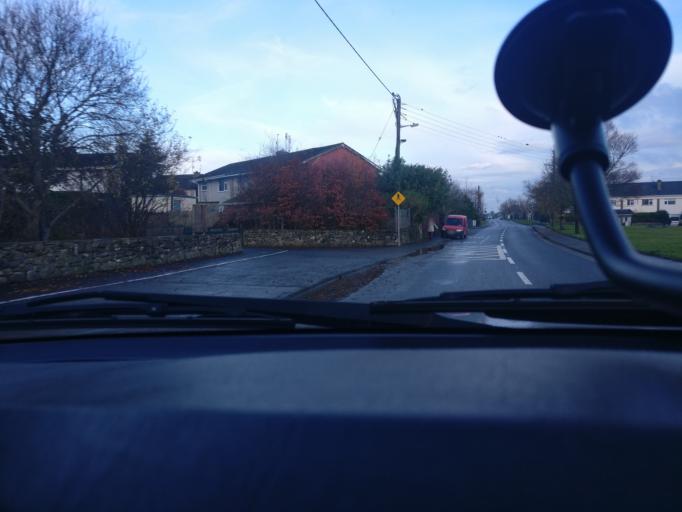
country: IE
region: Connaught
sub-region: County Galway
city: Loughrea
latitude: 53.1980
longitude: -8.5878
